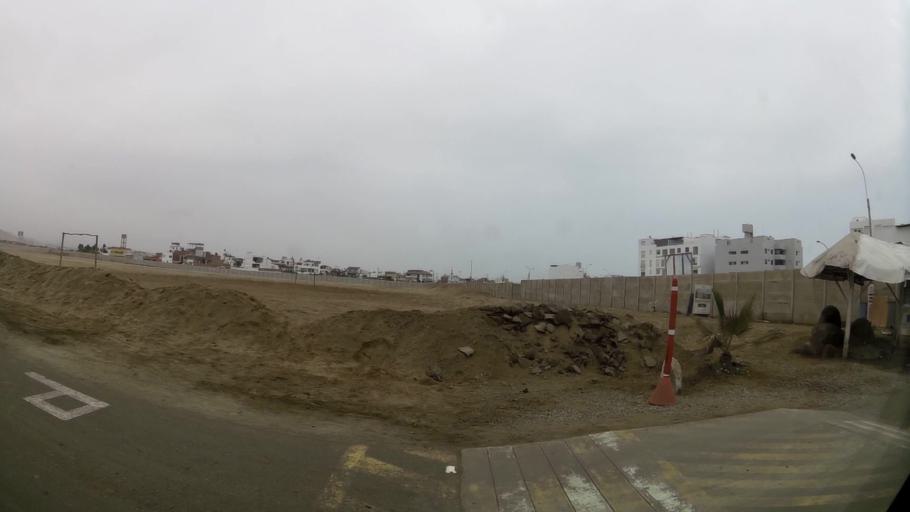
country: PE
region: Lima
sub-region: Lima
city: Punta Hermosa
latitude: -12.3275
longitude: -76.8310
